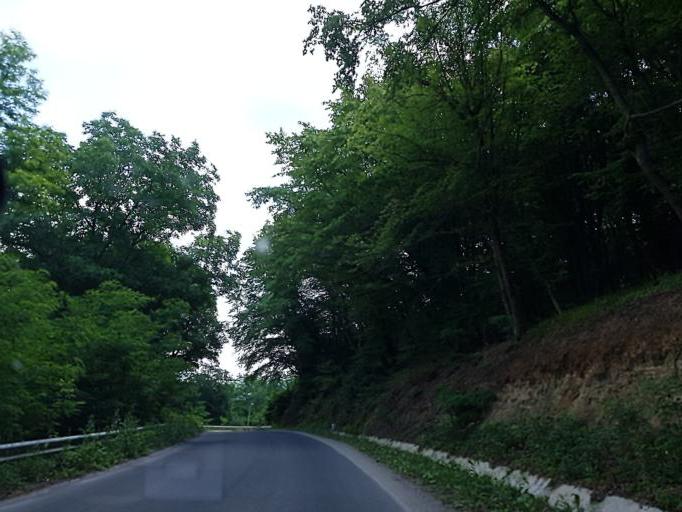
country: RO
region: Sibiu
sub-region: Comuna Seica Mare
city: Seica Mare
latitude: 46.0389
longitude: 24.1591
